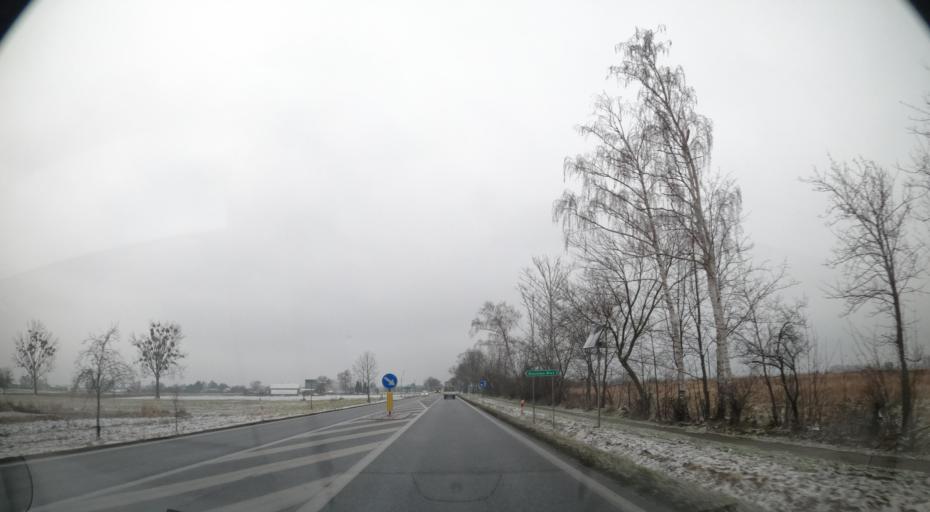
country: PL
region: Masovian Voivodeship
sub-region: Powiat sochaczewski
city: Paprotnia
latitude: 52.2065
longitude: 20.4900
